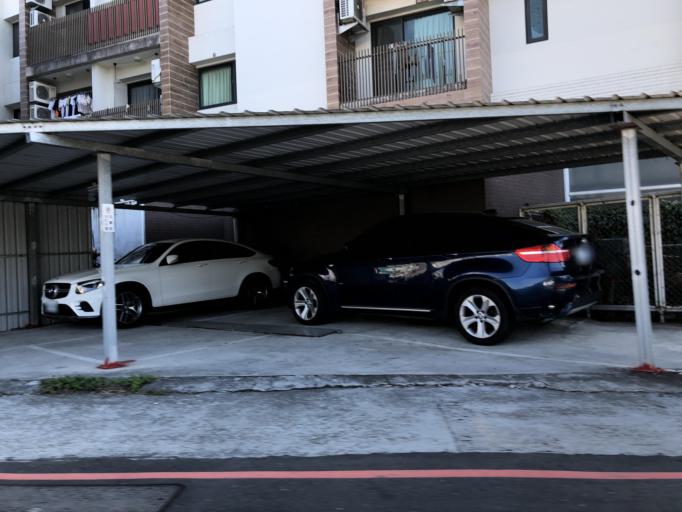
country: TW
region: Taiwan
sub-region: Tainan
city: Tainan
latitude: 23.0347
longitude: 120.3000
